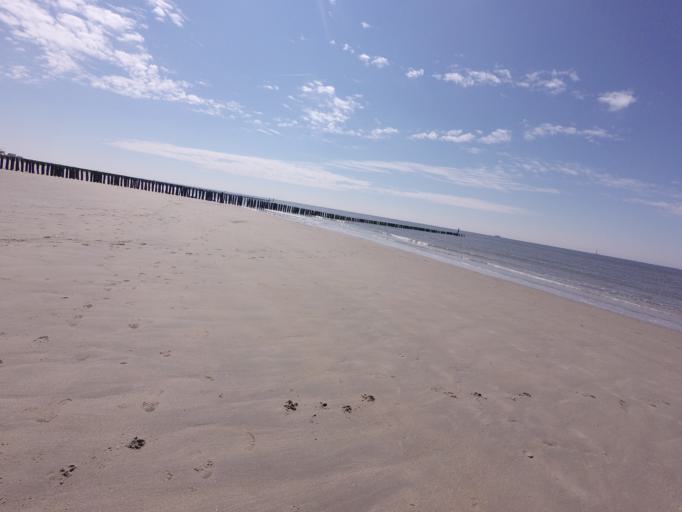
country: NL
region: Zeeland
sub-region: Gemeente Vlissingen
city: Vlissingen
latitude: 51.5157
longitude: 3.4487
